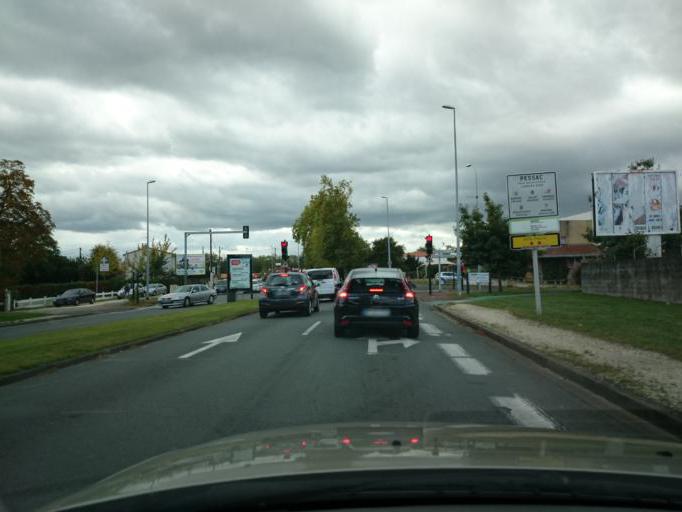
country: FR
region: Aquitaine
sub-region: Departement de la Gironde
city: Pessac
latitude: 44.8028
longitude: -0.6631
